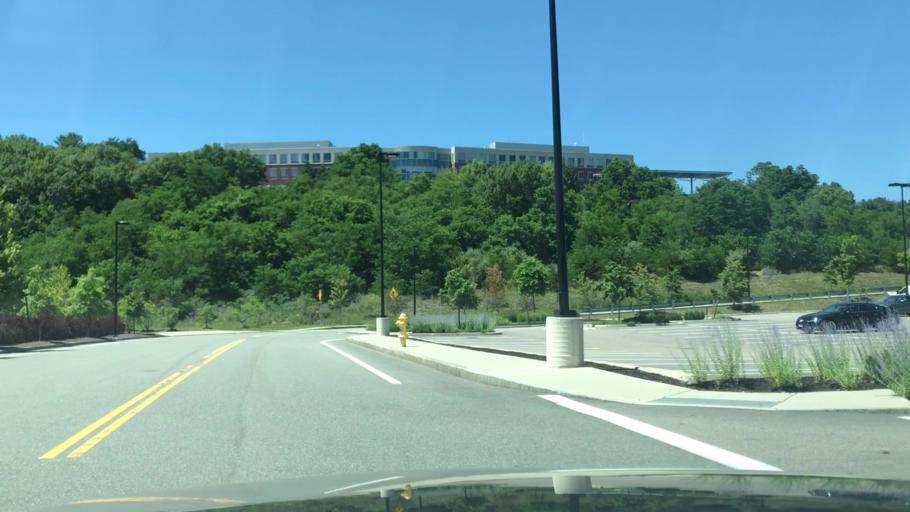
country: US
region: Massachusetts
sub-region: Norfolk County
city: Dedham
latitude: 42.2023
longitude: -71.1562
